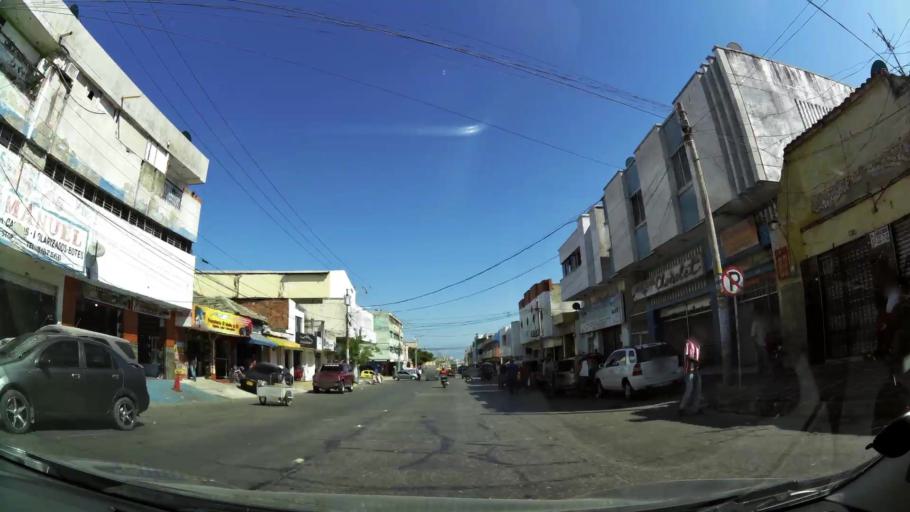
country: CO
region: Atlantico
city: Barranquilla
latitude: 10.9791
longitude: -74.7849
